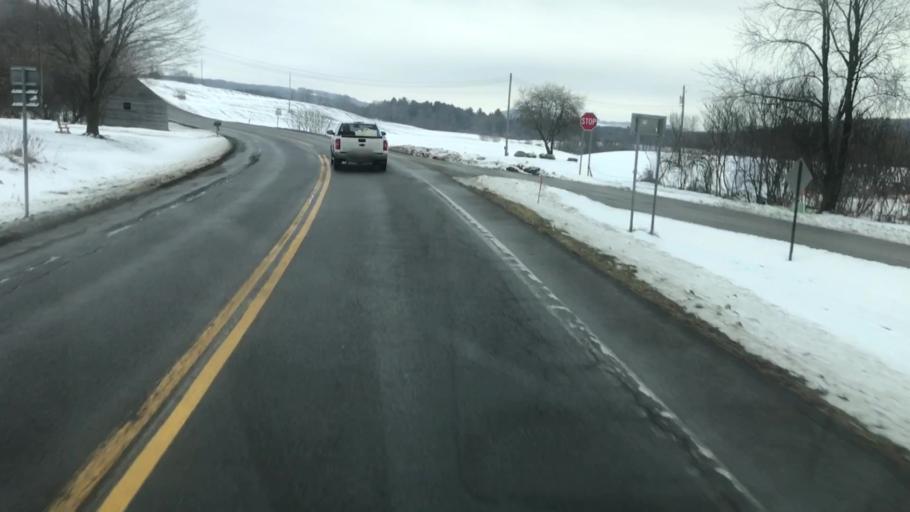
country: US
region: New York
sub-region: Cortland County
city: Cortland West
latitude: 42.6817
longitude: -76.3002
